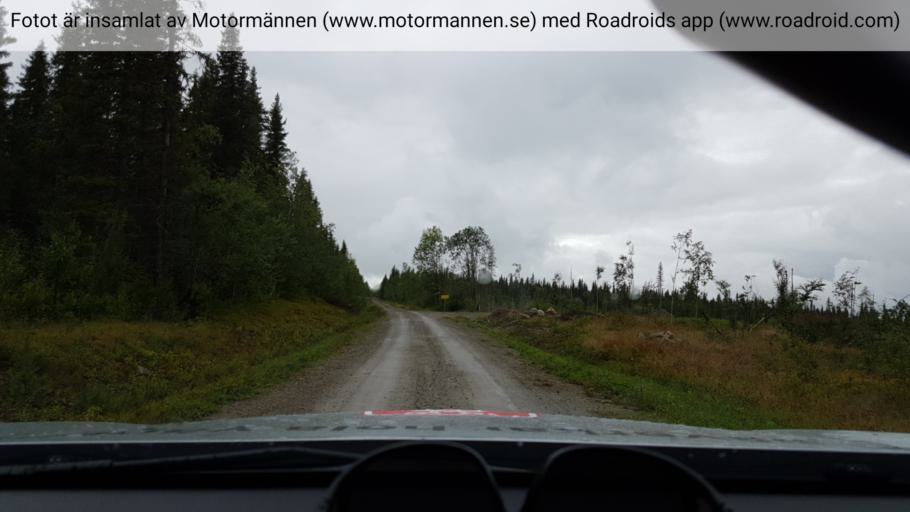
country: SE
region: Vaesterbotten
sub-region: Asele Kommun
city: Insjon
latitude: 64.8004
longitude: 17.4794
